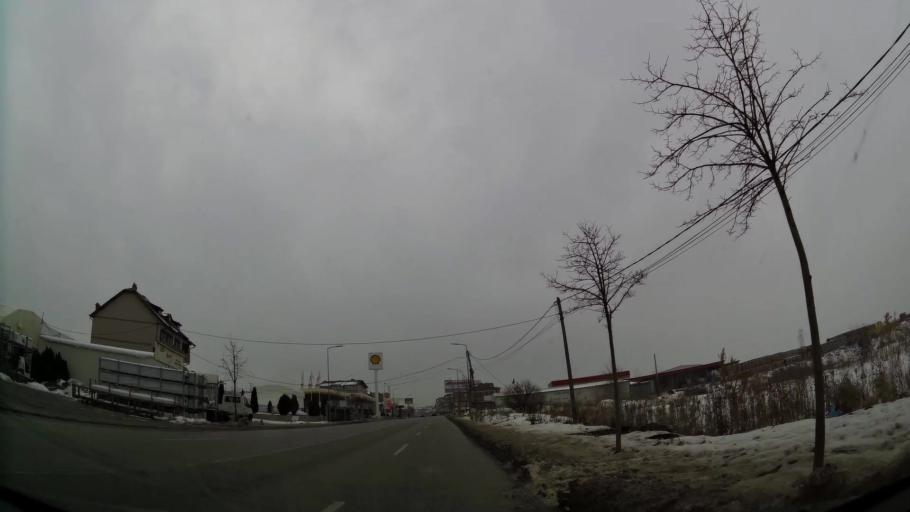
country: XK
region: Pristina
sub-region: Komuna e Prishtines
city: Pristina
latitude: 42.6988
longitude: 21.1593
